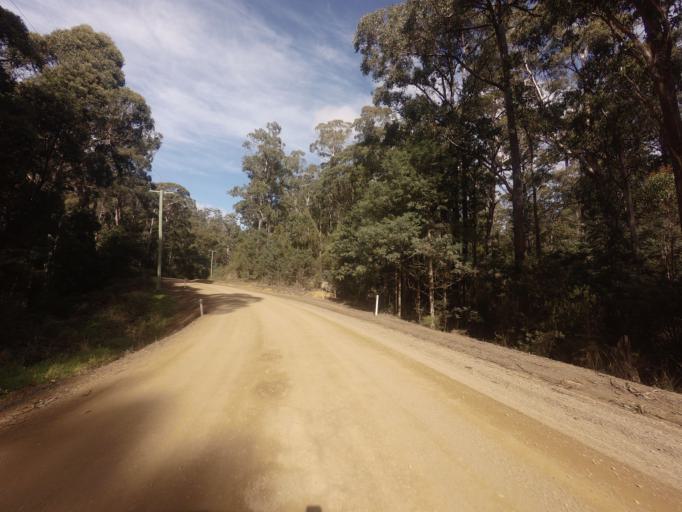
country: AU
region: Tasmania
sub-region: Clarence
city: Sandford
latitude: -43.1243
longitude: 147.7623
